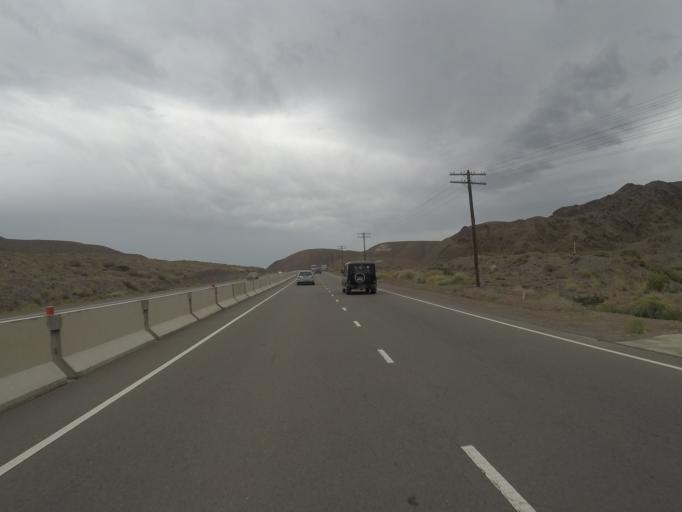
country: KG
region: Ysyk-Koel
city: Balykchy
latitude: 42.4637
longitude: 76.0008
